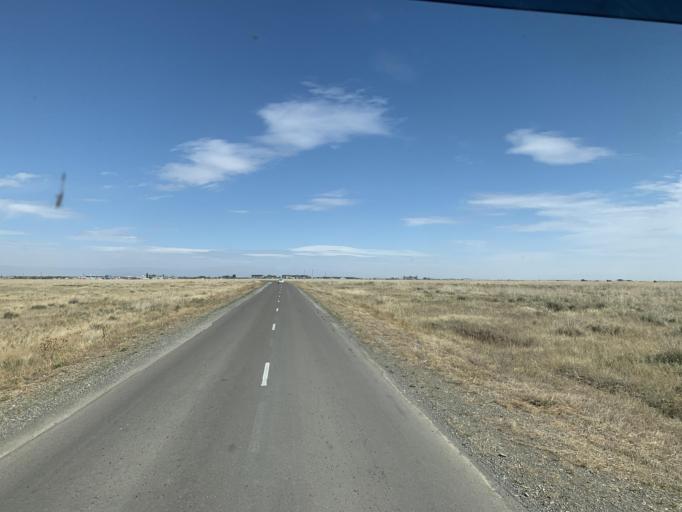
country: CN
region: Xinjiang Uygur Zizhiqu
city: Tacheng
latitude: 46.6676
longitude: 82.7642
